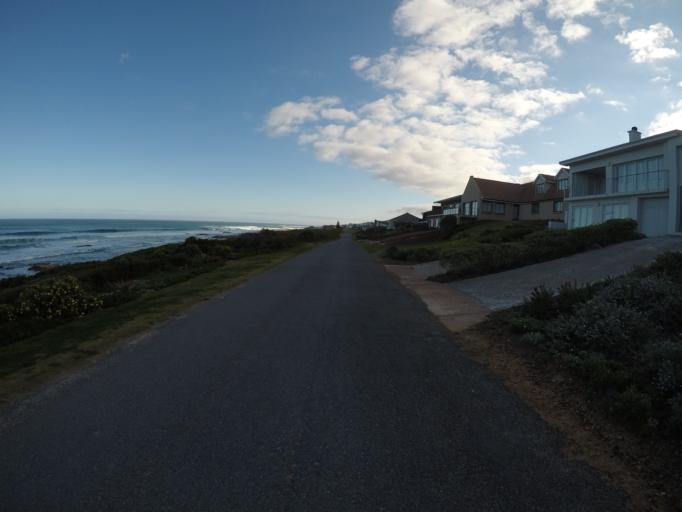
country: ZA
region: Western Cape
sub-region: Eden District Municipality
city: Riversdale
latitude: -34.4209
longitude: 21.3494
